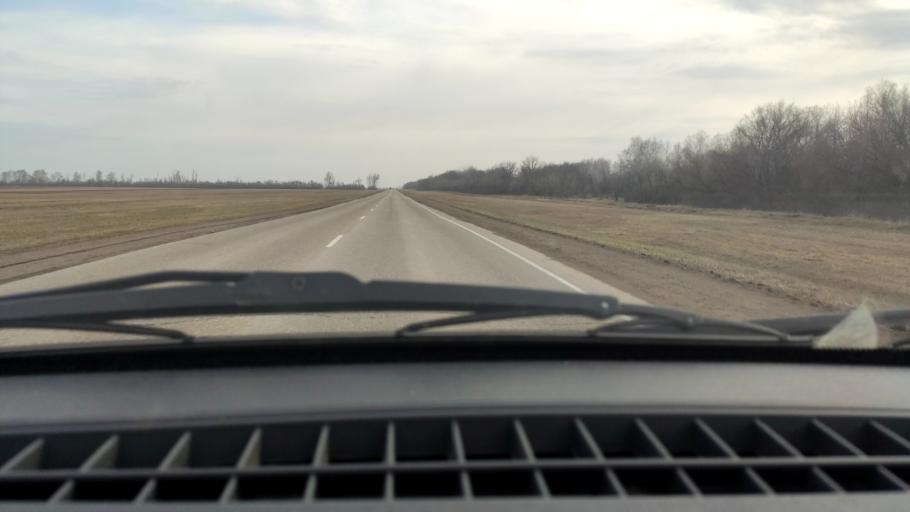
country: RU
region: Bashkortostan
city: Davlekanovo
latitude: 54.2608
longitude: 55.0900
